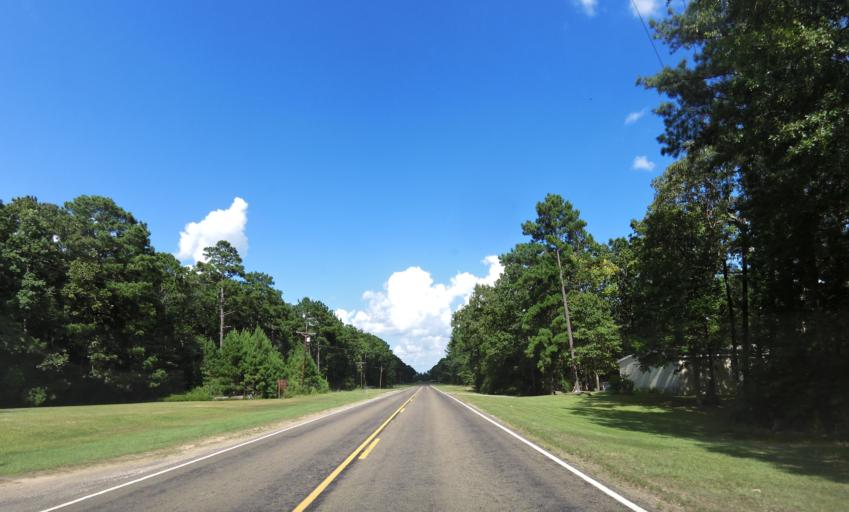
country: US
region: Louisiana
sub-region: Vernon Parish
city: New Llano
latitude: 31.1609
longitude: -93.5814
